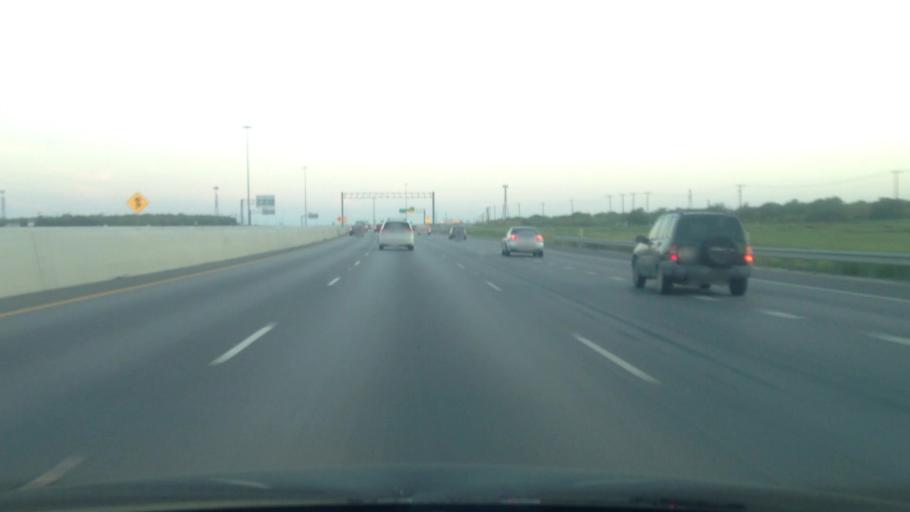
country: US
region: Texas
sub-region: Tarrant County
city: Blue Mound
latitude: 32.8831
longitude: -97.3177
